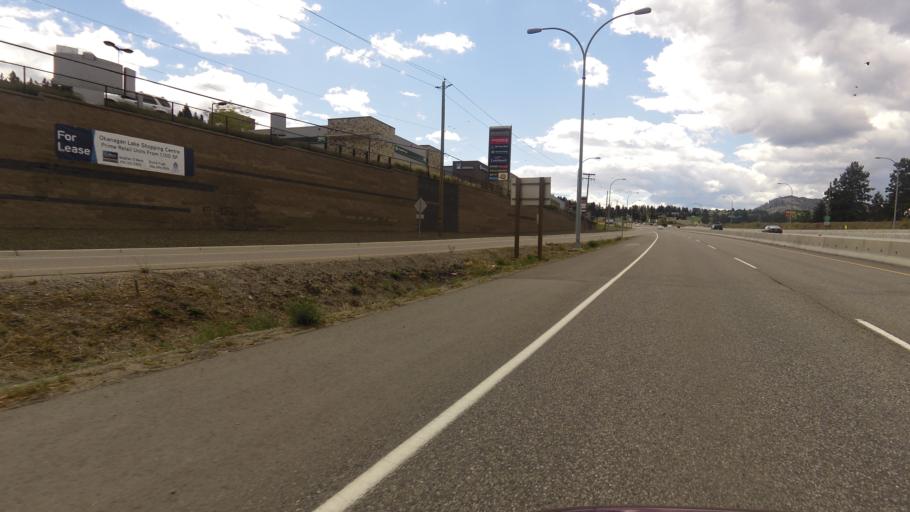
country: CA
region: British Columbia
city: West Kelowna
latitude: 49.8806
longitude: -119.5368
